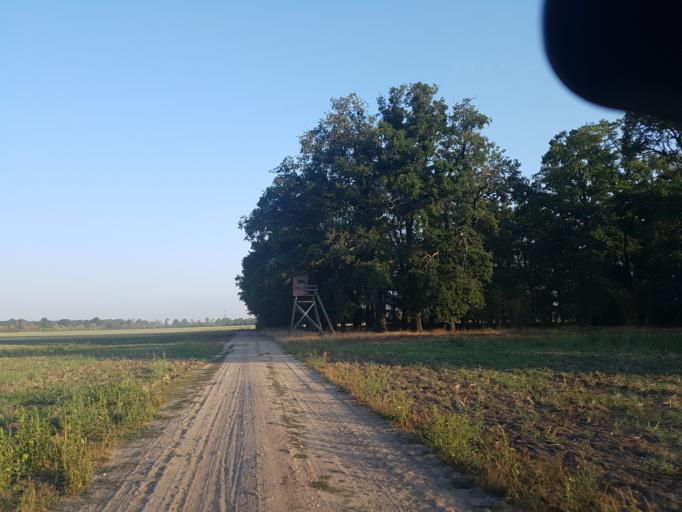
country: DE
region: Brandenburg
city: Herzberg
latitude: 51.6533
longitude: 13.2830
